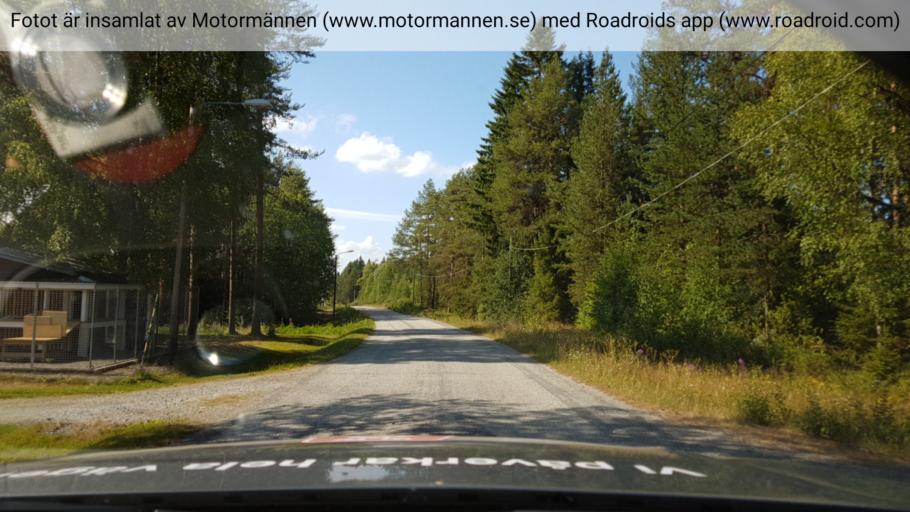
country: SE
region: Vaesterbotten
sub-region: Dorotea Kommun
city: Dorotea
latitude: 64.0979
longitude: 16.4153
